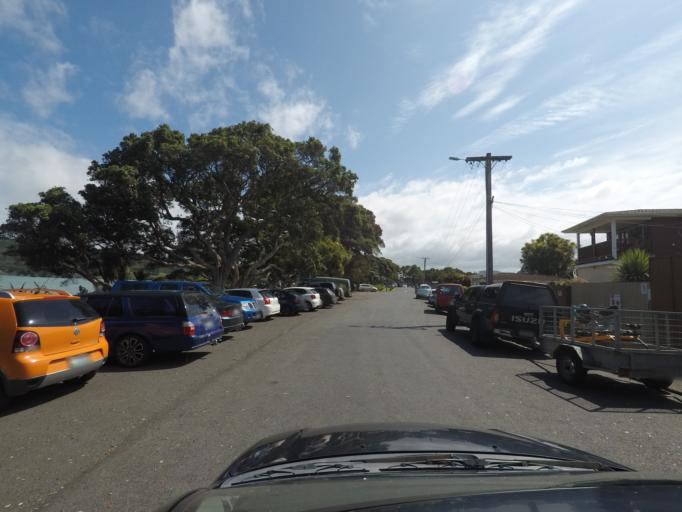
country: NZ
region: Waikato
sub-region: Waikato District
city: Raglan
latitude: -37.7992
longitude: 174.8673
